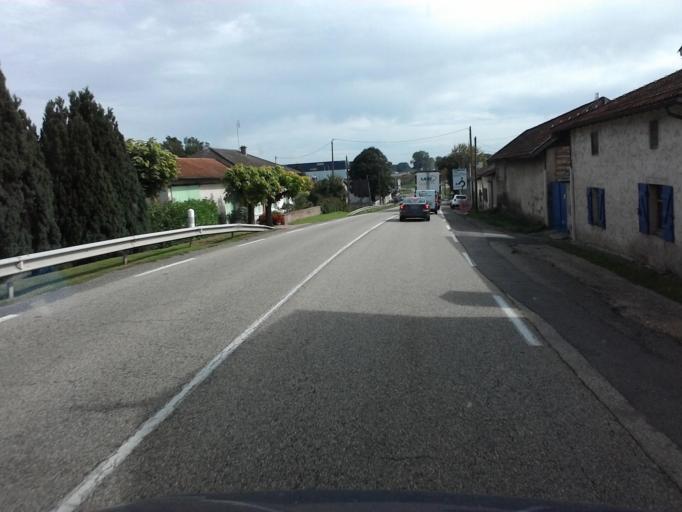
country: FR
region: Rhone-Alpes
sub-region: Departement de l'Ain
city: Crottet
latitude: 46.2889
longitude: 4.9167
